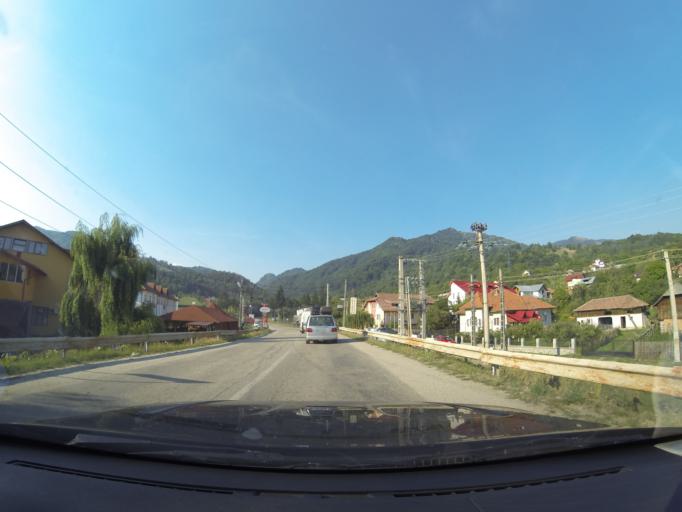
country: RO
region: Arges
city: Poenari
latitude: 45.3342
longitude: 24.6359
